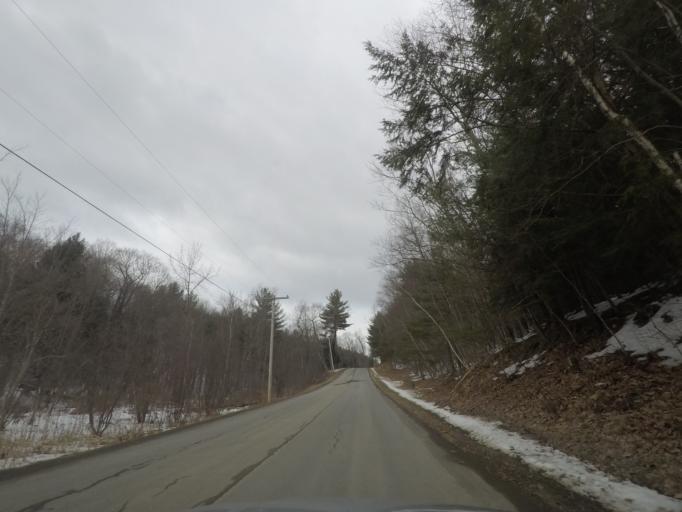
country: US
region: New York
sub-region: Saratoga County
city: Waterford
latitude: 42.7710
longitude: -73.6109
